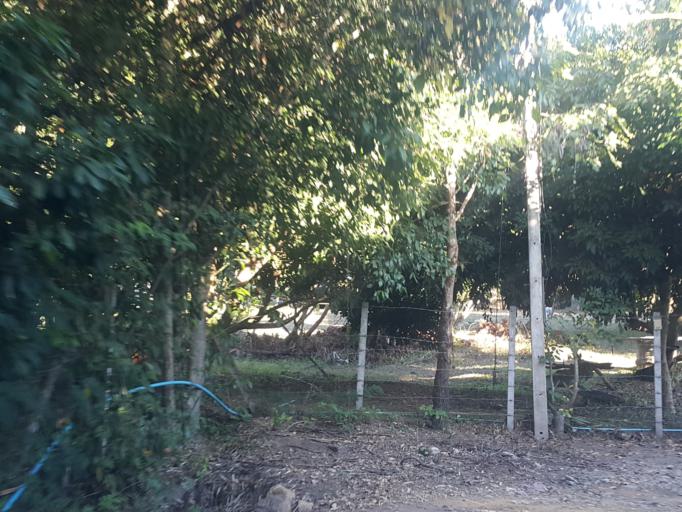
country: TH
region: Chiang Mai
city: San Sai
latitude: 18.9290
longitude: 99.1457
